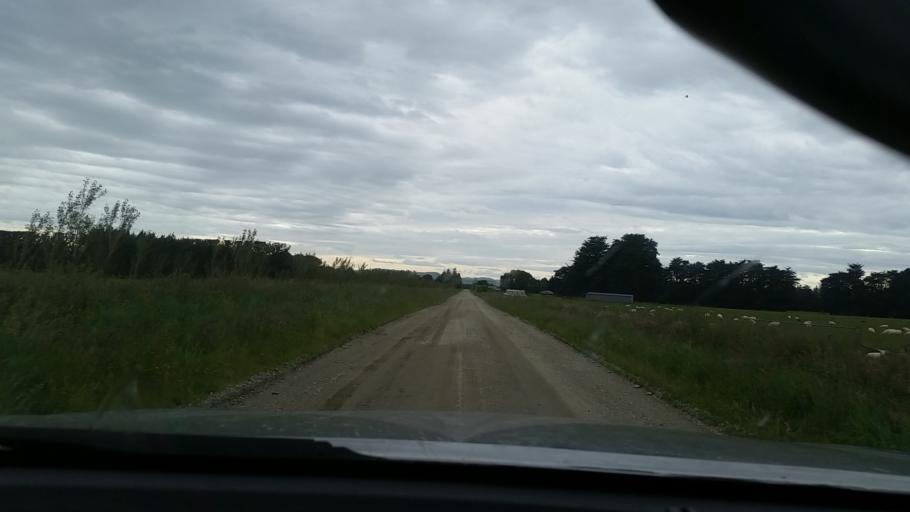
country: NZ
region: Southland
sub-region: Gore District
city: Gore
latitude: -46.2842
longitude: 168.7747
